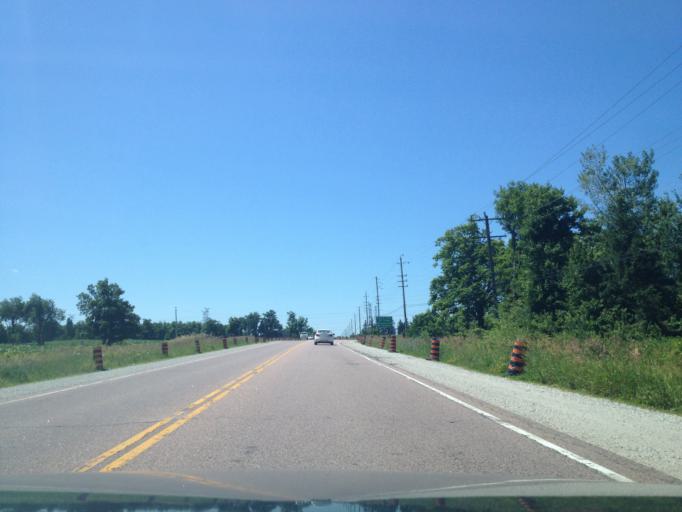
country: CA
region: Ontario
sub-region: Halton
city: Milton
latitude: 43.6578
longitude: -80.0055
